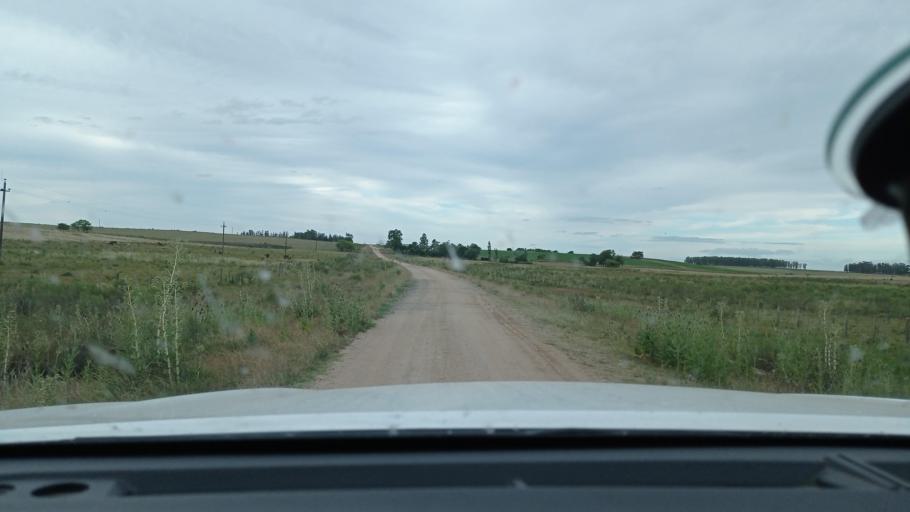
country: UY
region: Florida
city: Casupa
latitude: -34.1223
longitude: -55.7720
